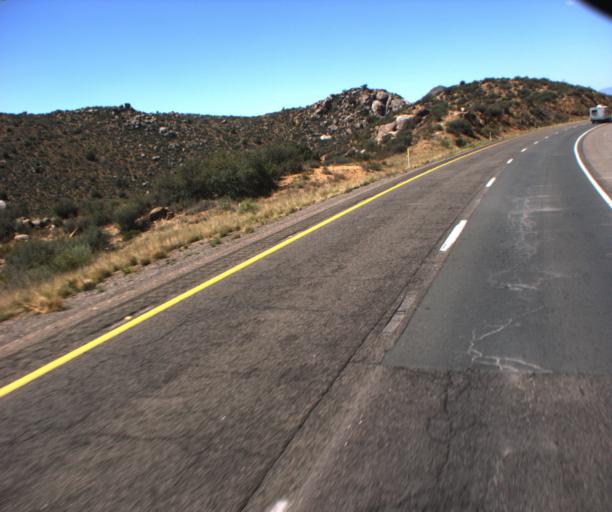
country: US
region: Arizona
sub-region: Mohave County
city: Peach Springs
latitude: 35.1750
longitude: -113.5017
